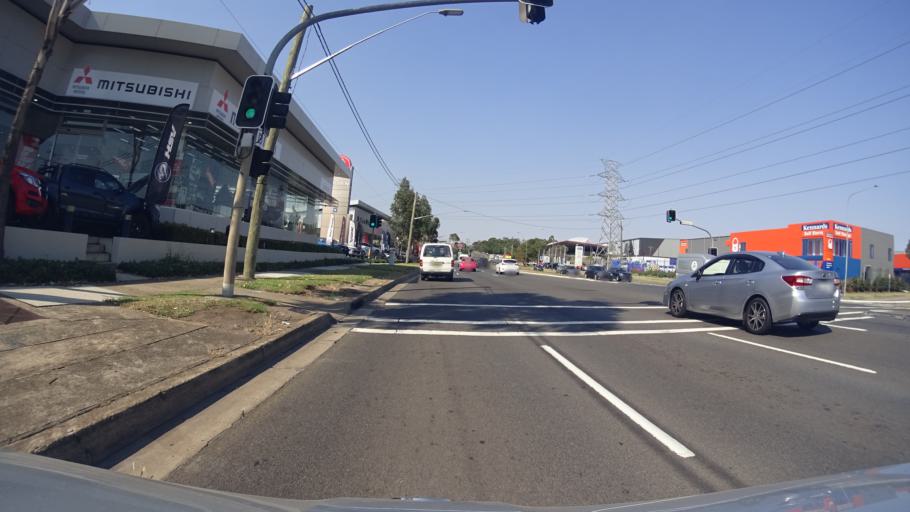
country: AU
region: New South Wales
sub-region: Strathfield
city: Strathfield South
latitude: -33.8904
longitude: 151.0593
